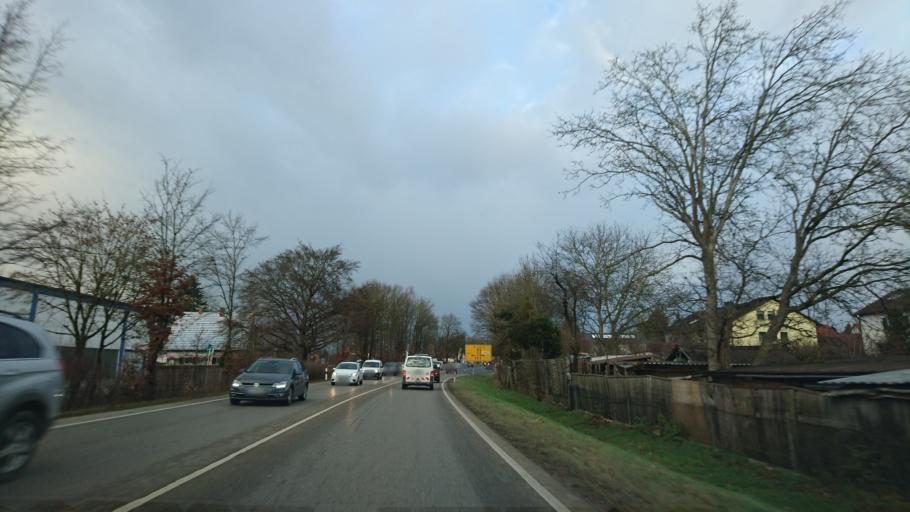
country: DE
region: Bavaria
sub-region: Swabia
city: Diedorf
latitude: 48.3679
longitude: 10.7952
